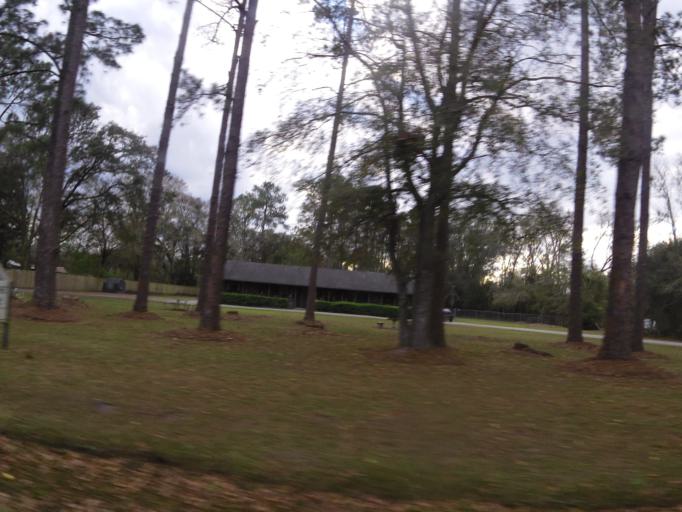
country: US
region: Florida
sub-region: Saint Johns County
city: Fruit Cove
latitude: 30.2021
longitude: -81.5834
